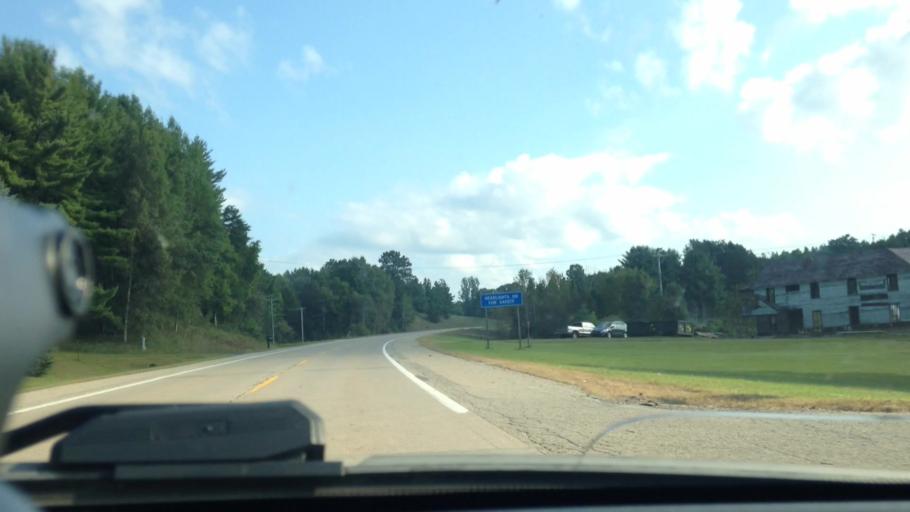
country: US
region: Michigan
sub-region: Dickinson County
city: Norway
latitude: 45.7619
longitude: -87.9205
